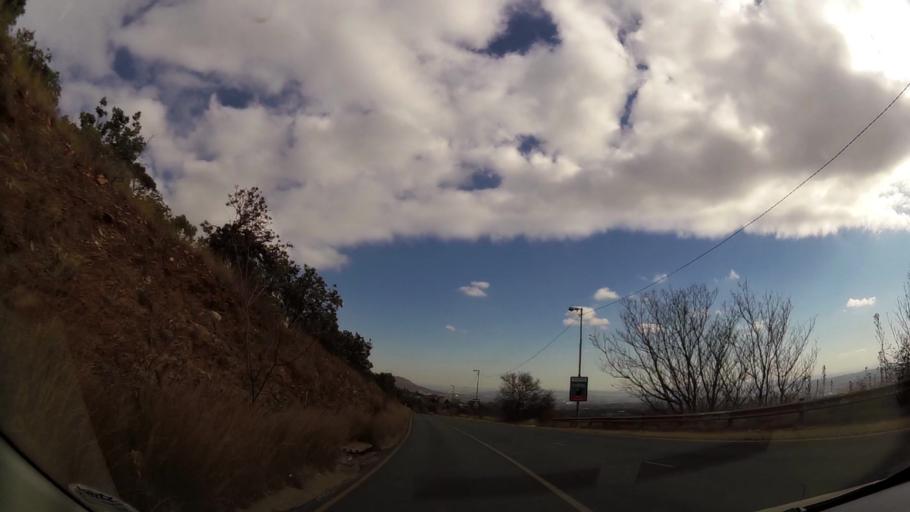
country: ZA
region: Gauteng
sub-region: City of Johannesburg Metropolitan Municipality
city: Roodepoort
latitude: -26.1036
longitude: 27.8657
